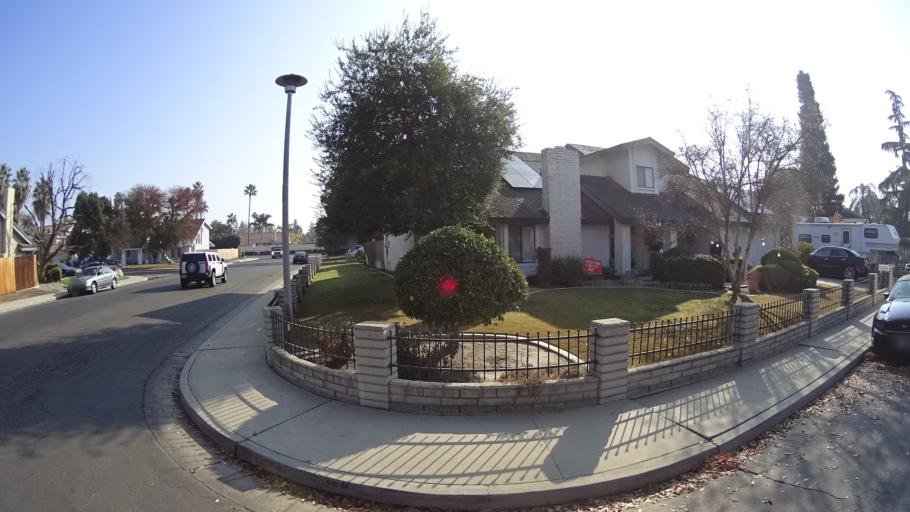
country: US
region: California
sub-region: Kern County
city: Greenacres
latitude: 35.3368
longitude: -119.0868
